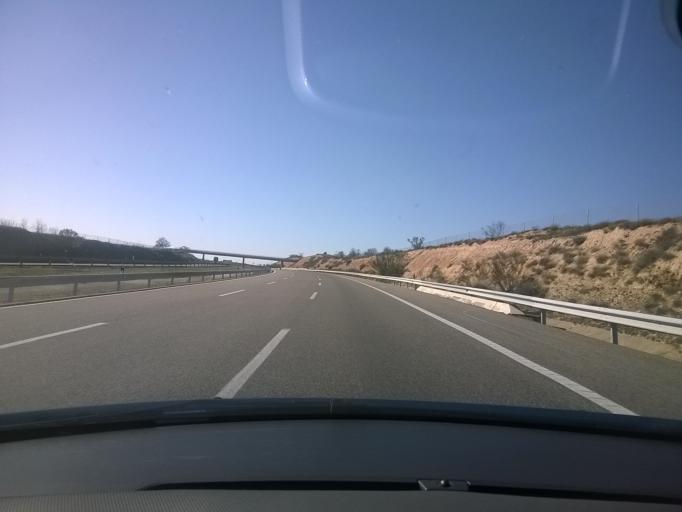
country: ES
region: Aragon
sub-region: Provincia de Huesca
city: Fraga
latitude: 41.4654
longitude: 0.2855
